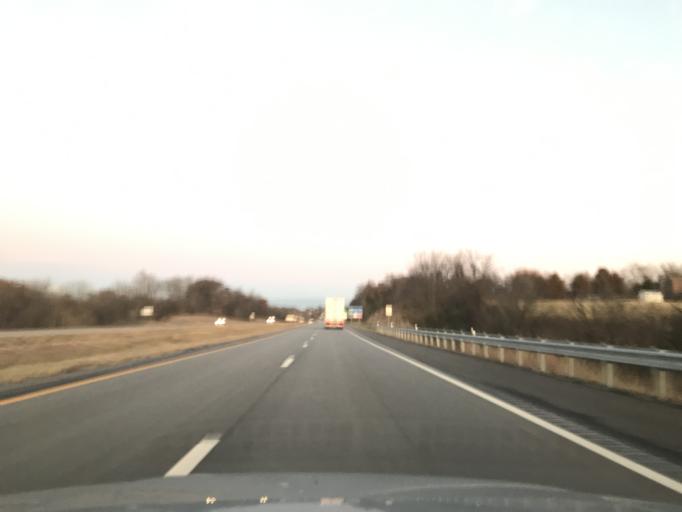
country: US
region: Missouri
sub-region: Marion County
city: Hannibal
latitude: 39.7143
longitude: -91.4100
